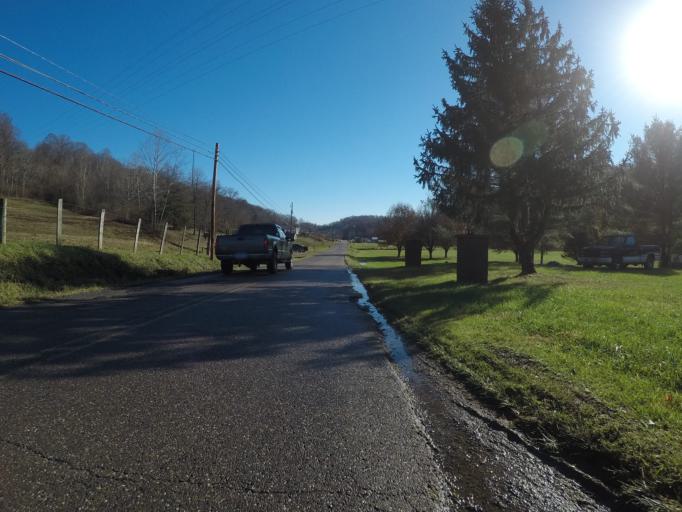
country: US
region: West Virginia
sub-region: Cabell County
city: Huntington
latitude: 38.4821
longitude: -82.4781
